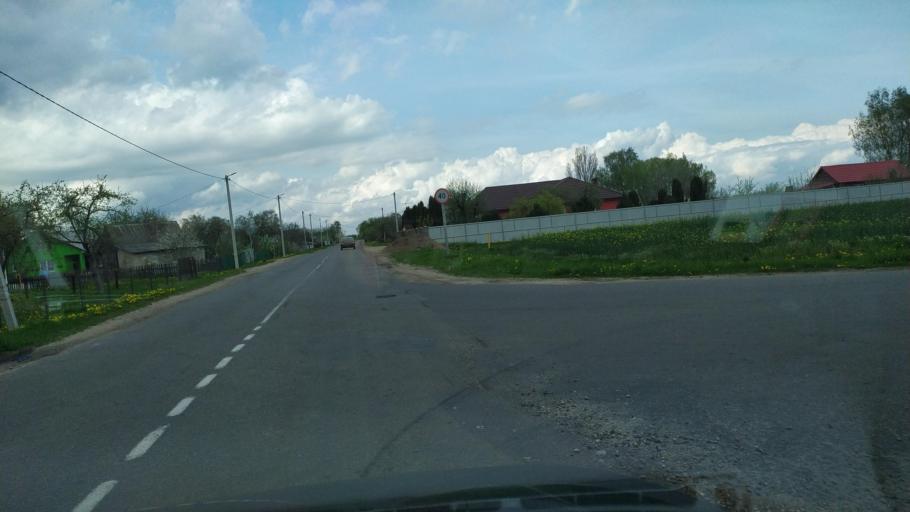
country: BY
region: Brest
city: Pruzhany
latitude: 52.5882
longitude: 24.4102
